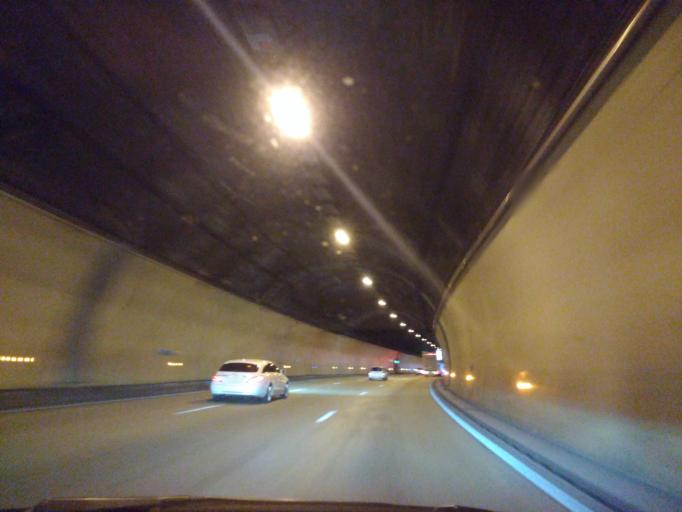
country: FR
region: Provence-Alpes-Cote d'Azur
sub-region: Departement des Alpes-Maritimes
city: Colomars
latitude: 43.7181
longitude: 7.2139
